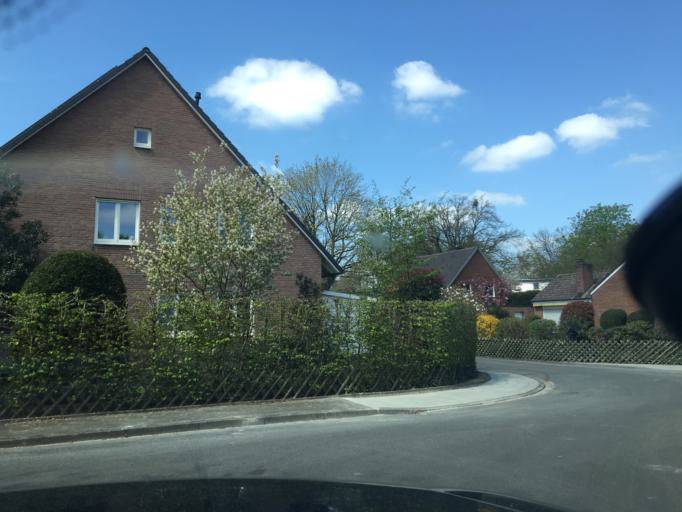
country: DE
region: North Rhine-Westphalia
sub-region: Regierungsbezirk Munster
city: Muenster
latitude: 51.9827
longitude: 7.6432
